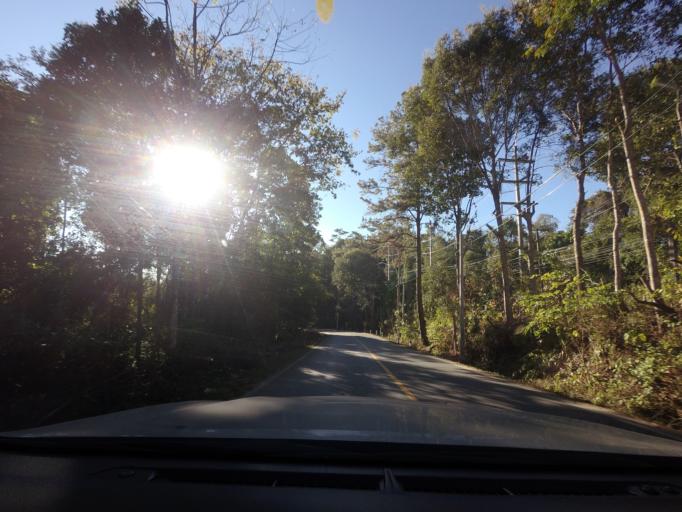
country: TH
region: Mae Hong Son
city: Mae Hi
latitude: 19.2772
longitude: 98.6006
